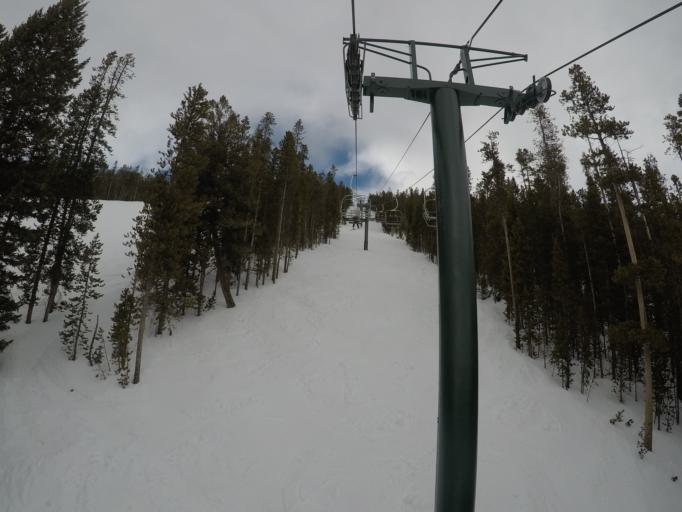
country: US
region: Montana
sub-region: Granite County
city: Philipsburg
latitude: 46.2564
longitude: -113.2440
